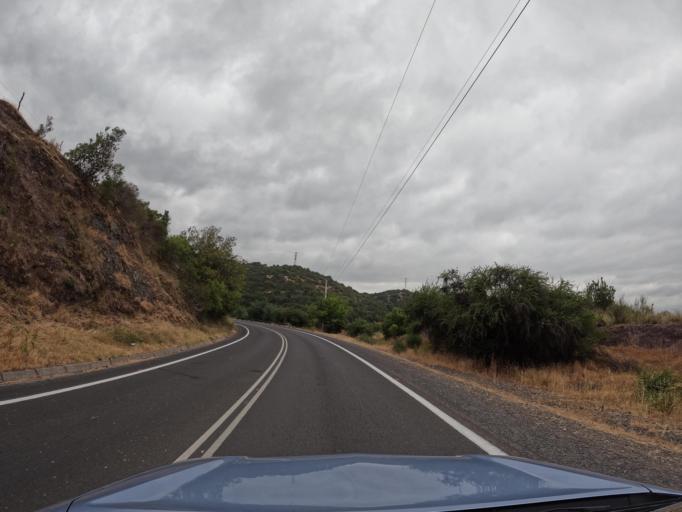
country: CL
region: O'Higgins
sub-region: Provincia de Colchagua
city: Chimbarongo
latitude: -34.7295
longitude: -71.1061
